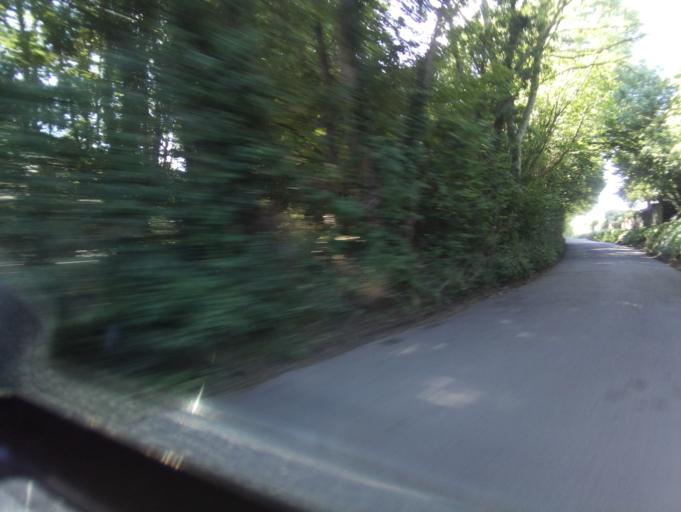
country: GB
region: England
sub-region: Herefordshire
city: Ross on Wye
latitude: 51.9265
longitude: -2.5828
